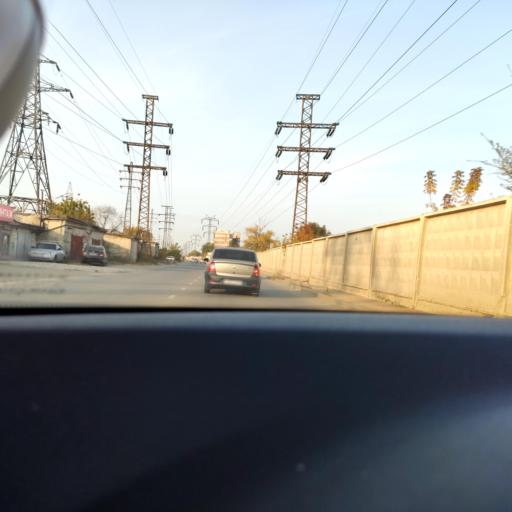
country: RU
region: Samara
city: Petra-Dubrava
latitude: 53.2437
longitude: 50.2913
